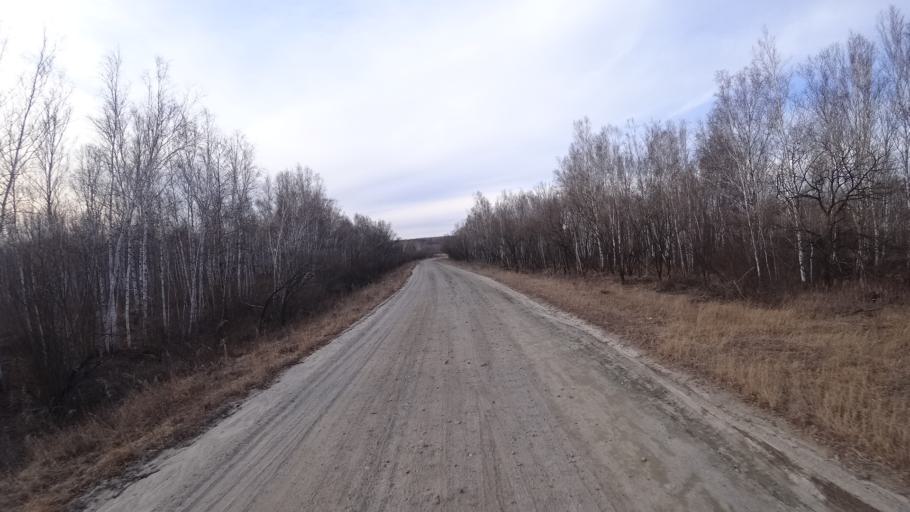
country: RU
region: Amur
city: Bureya
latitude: 50.0154
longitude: 129.7743
